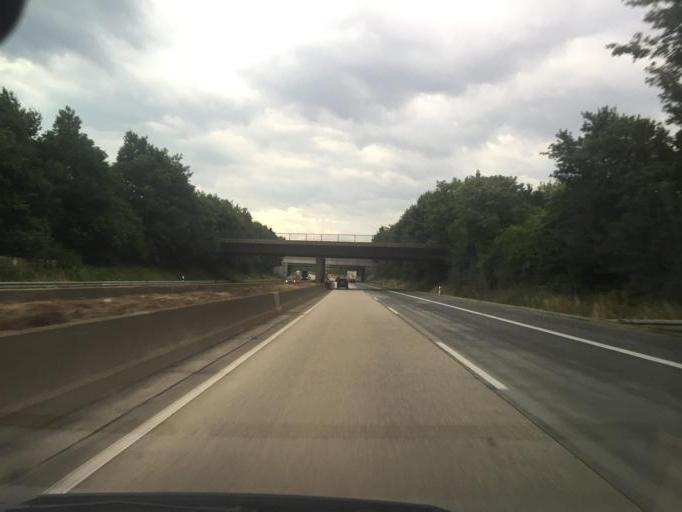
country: DE
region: North Rhine-Westphalia
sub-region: Regierungsbezirk Koln
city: Bedburg
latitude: 50.9683
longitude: 6.5645
